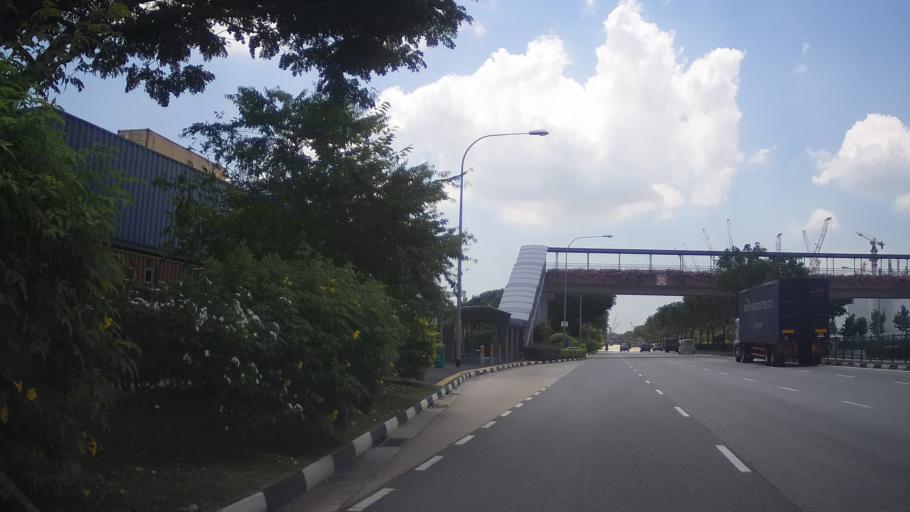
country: MY
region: Johor
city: Johor Bahru
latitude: 1.3194
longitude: 103.6791
